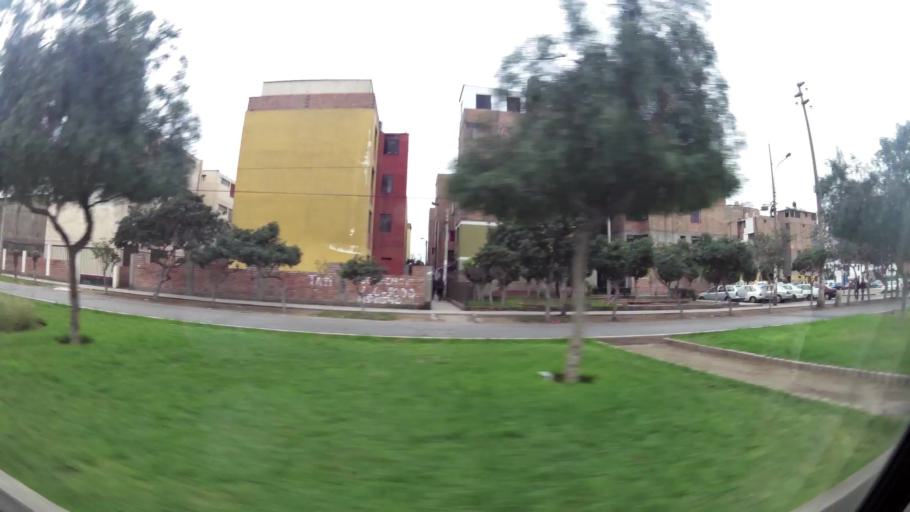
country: PE
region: Lima
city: Lima
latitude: -12.0591
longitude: -77.0634
